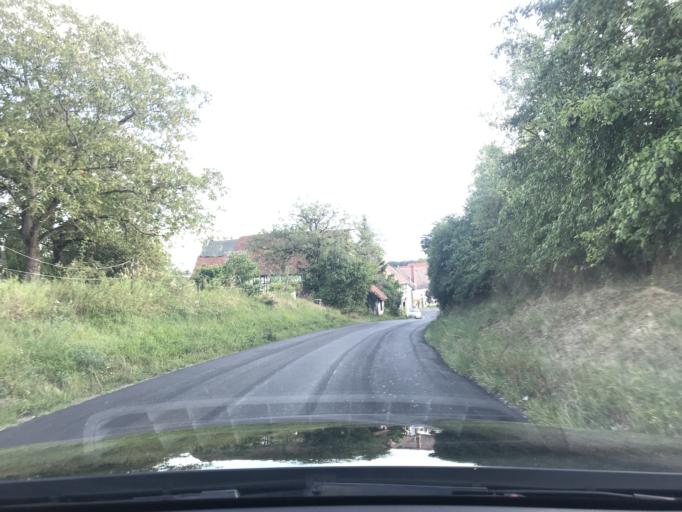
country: DE
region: Bavaria
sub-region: Regierungsbezirk Unterfranken
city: Kirchlauter
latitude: 50.0630
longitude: 10.6736
